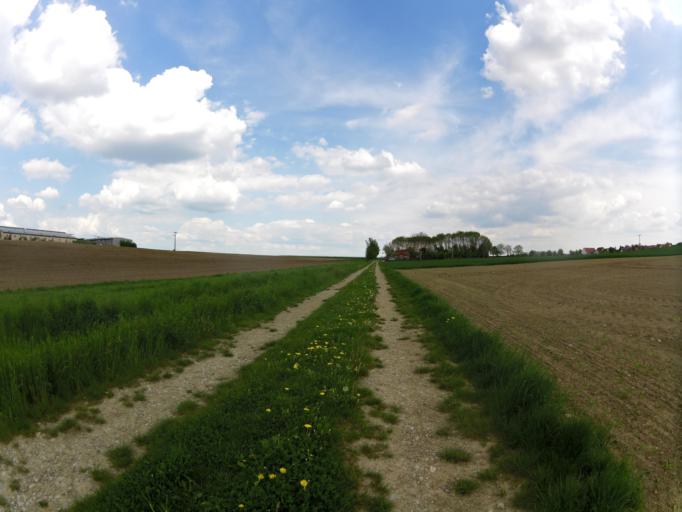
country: DE
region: Bavaria
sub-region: Regierungsbezirk Unterfranken
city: Giebelstadt
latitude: 49.6168
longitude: 9.9423
